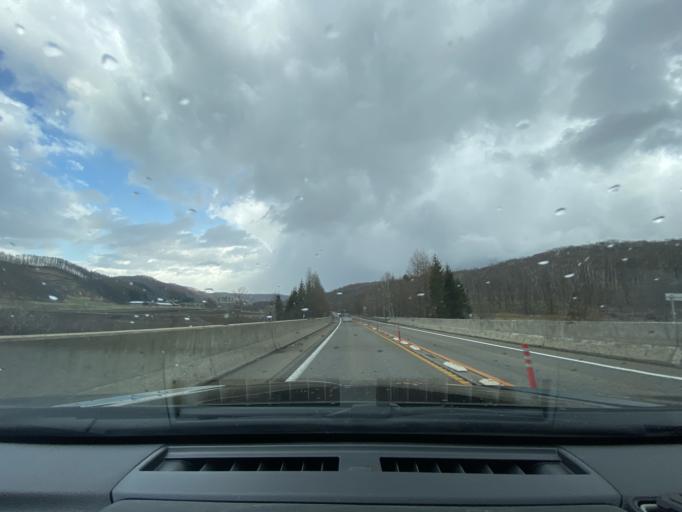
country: JP
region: Hokkaido
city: Otofuke
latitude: 42.9886
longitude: 143.2869
